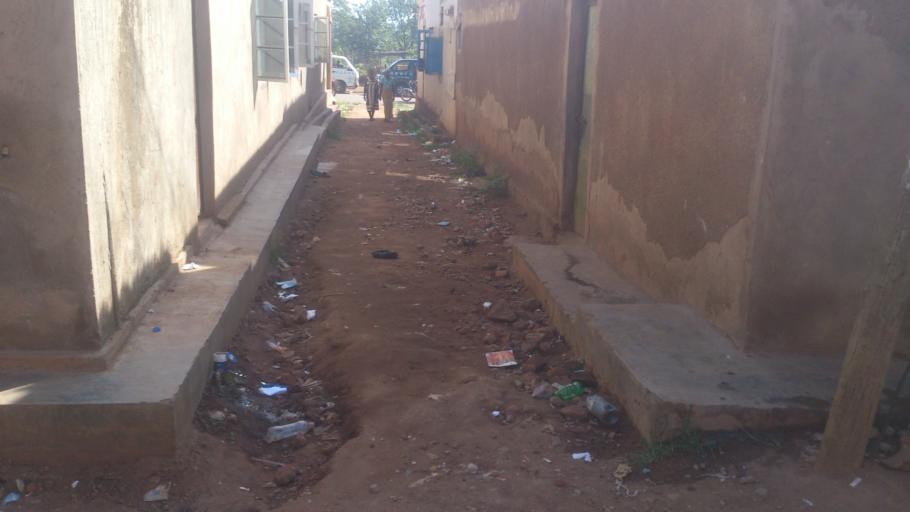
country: UG
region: Eastern Region
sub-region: Mbale District
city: Mbale
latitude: 1.0755
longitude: 34.1767
